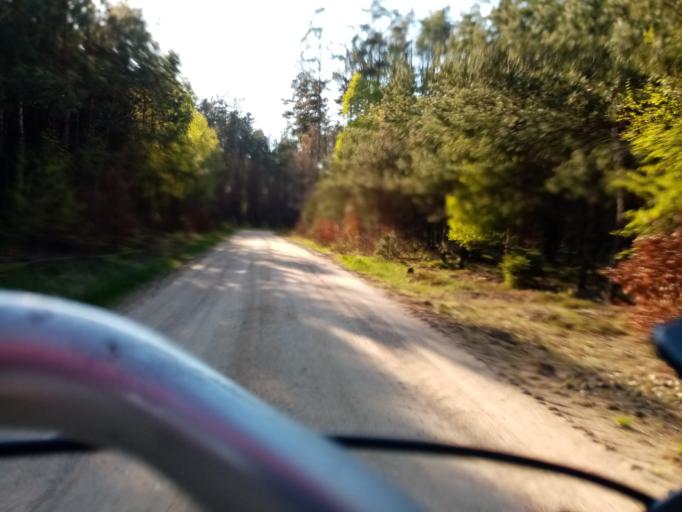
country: PL
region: Kujawsko-Pomorskie
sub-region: Powiat brodnicki
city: Gorzno
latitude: 53.1575
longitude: 19.6957
